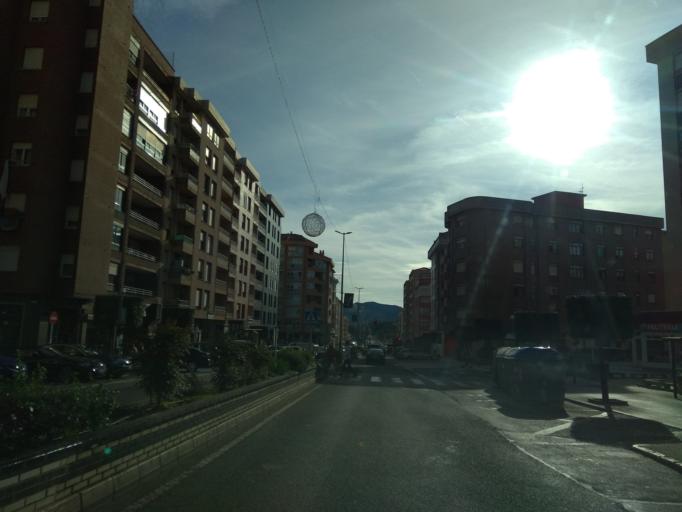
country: ES
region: Cantabria
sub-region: Provincia de Cantabria
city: El Astillero
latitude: 43.4185
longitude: -3.8459
